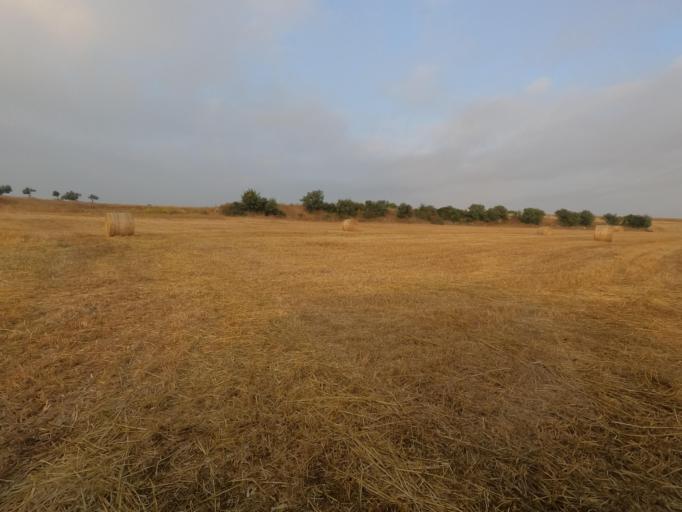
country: CY
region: Larnaka
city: Tersefanou
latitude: 34.8292
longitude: 33.5211
